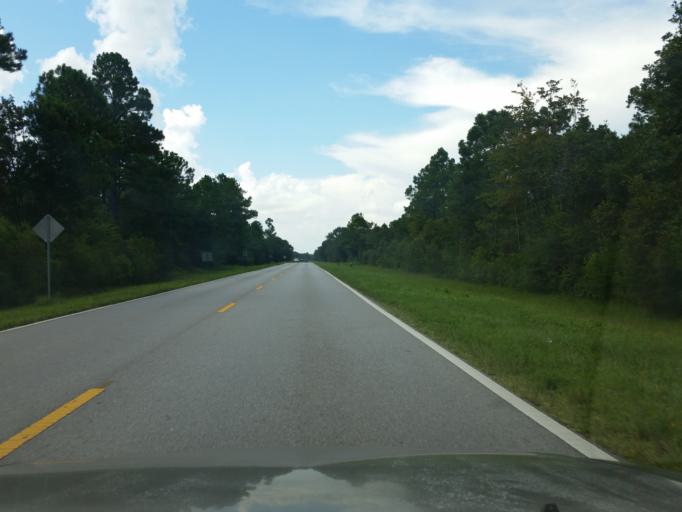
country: US
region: Florida
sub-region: Escambia County
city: Myrtle Grove
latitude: 30.3829
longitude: -87.4022
